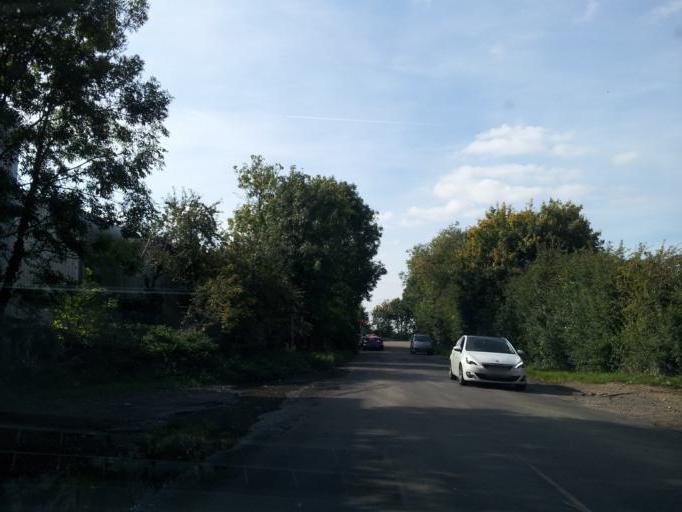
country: GB
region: England
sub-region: Cambridgeshire
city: Waterbeach
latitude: 52.2715
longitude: 0.1796
